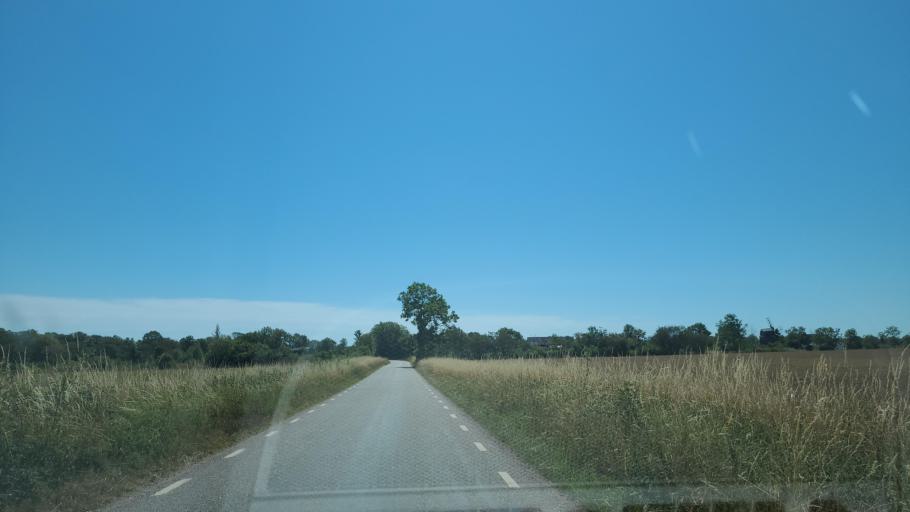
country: SE
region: Kalmar
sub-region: Borgholms Kommun
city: Borgholm
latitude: 56.7424
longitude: 16.7052
